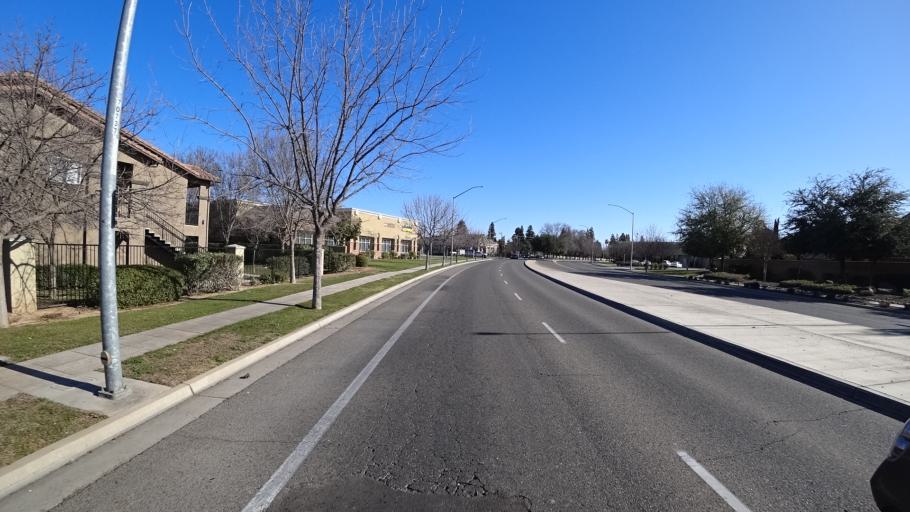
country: US
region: California
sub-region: Fresno County
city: West Park
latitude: 36.8289
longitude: -119.8679
